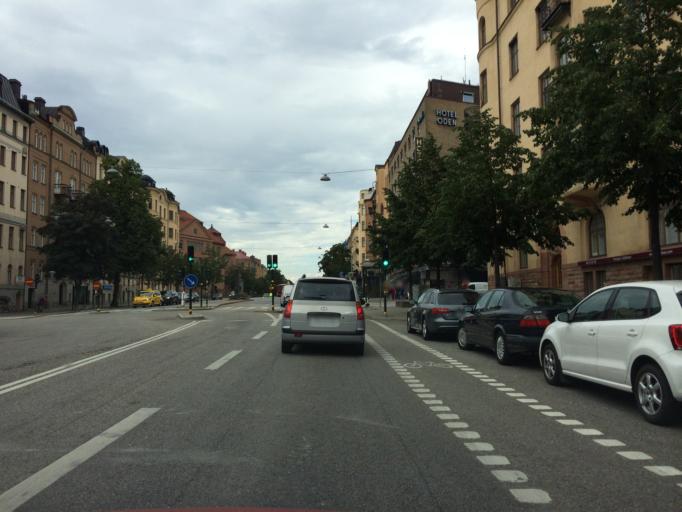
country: SE
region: Stockholm
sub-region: Stockholms Kommun
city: Stockholm
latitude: 59.3430
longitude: 18.0471
